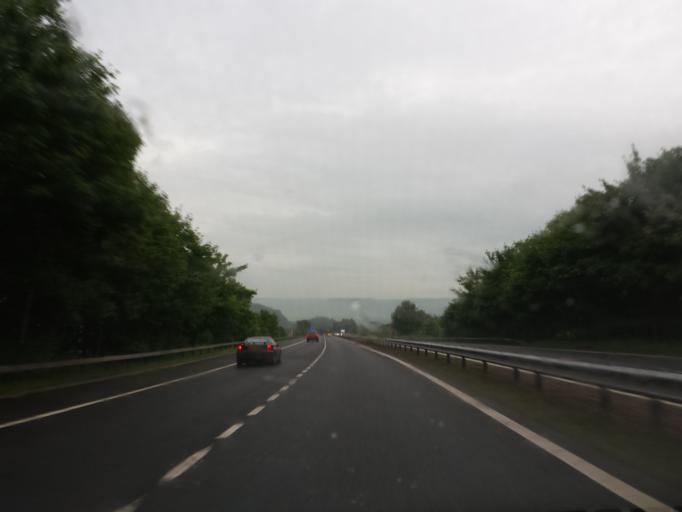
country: GB
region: Scotland
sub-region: Perth and Kinross
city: Perth
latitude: 56.3730
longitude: -3.4431
